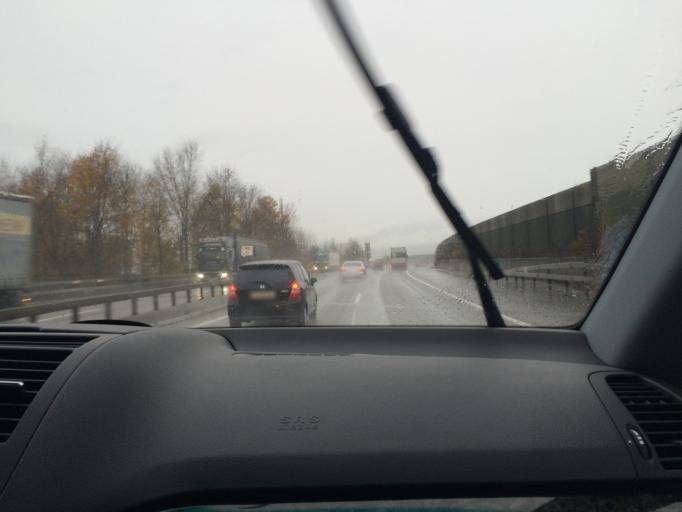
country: CH
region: Bern
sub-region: Emmental District
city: Kirchberg
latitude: 47.0906
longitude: 7.5731
